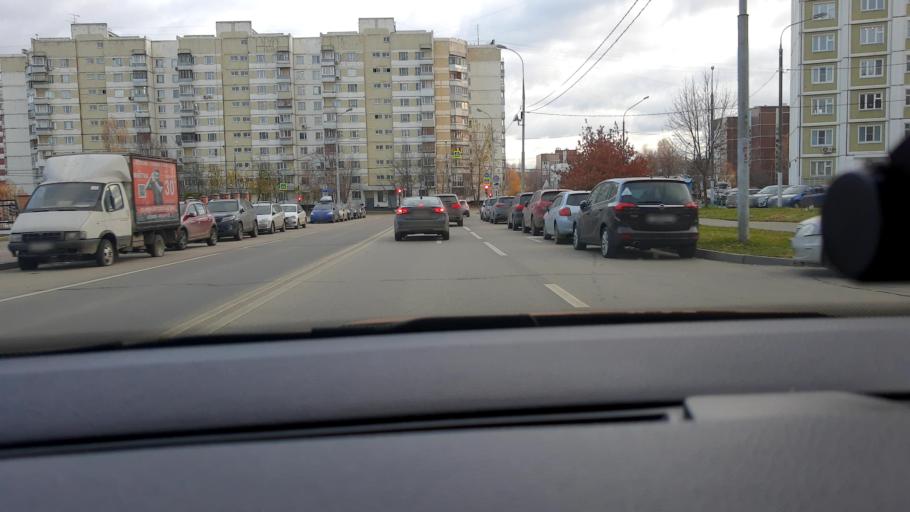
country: RU
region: Moskovskaya
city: Shcherbinka
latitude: 55.5449
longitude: 37.5410
